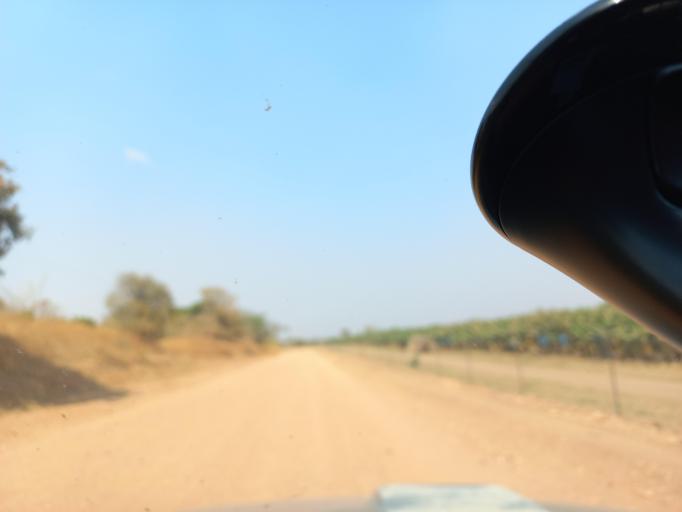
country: ZW
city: Chirundu
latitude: -15.9308
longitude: 28.9608
